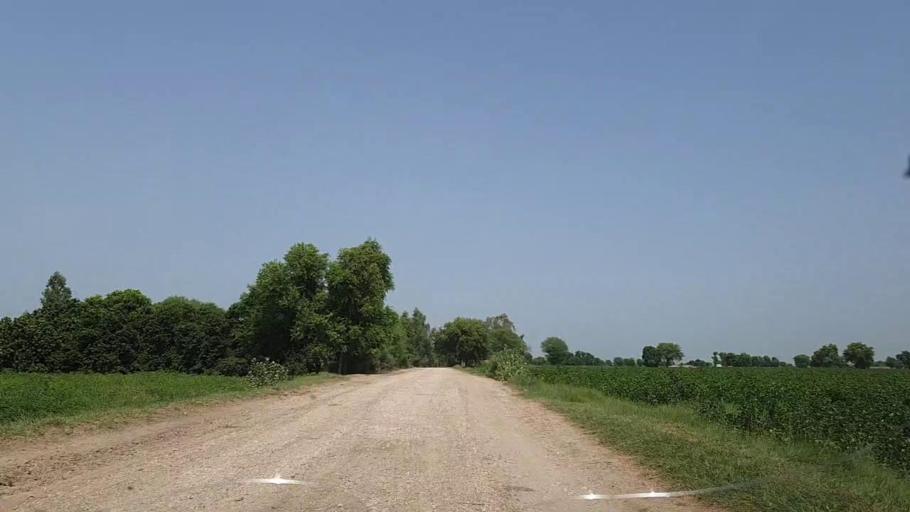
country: PK
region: Sindh
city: Tharu Shah
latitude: 27.0136
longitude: 68.1346
